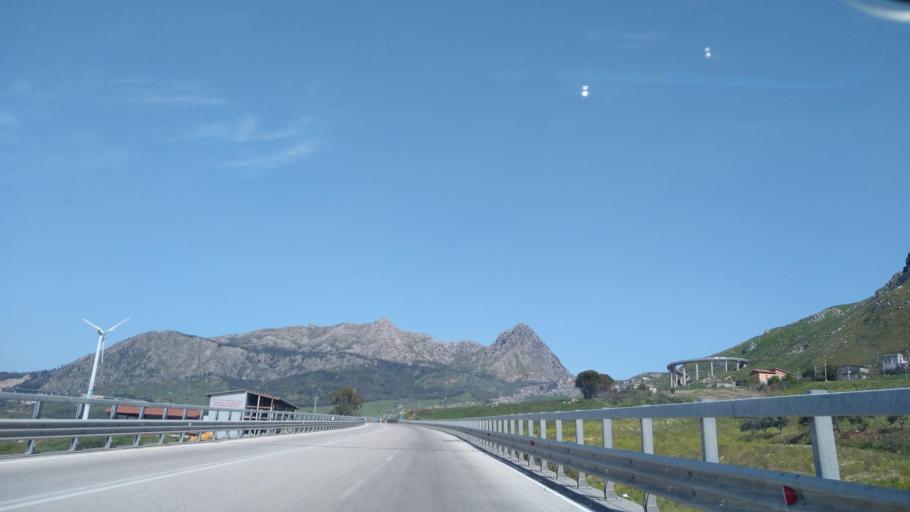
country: IT
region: Sicily
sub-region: Palermo
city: San Giuseppe Jato
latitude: 37.9765
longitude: 13.2161
